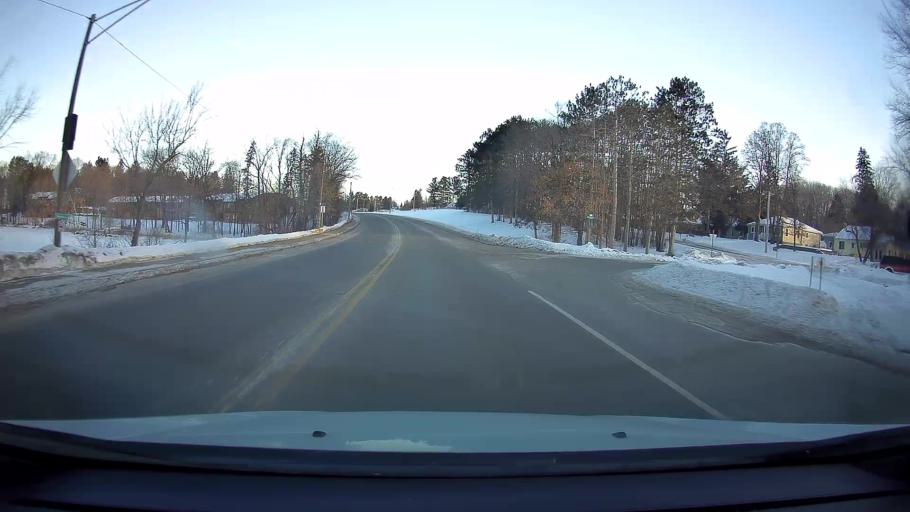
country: US
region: Wisconsin
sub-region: Barron County
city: Cumberland
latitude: 45.5443
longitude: -92.0178
